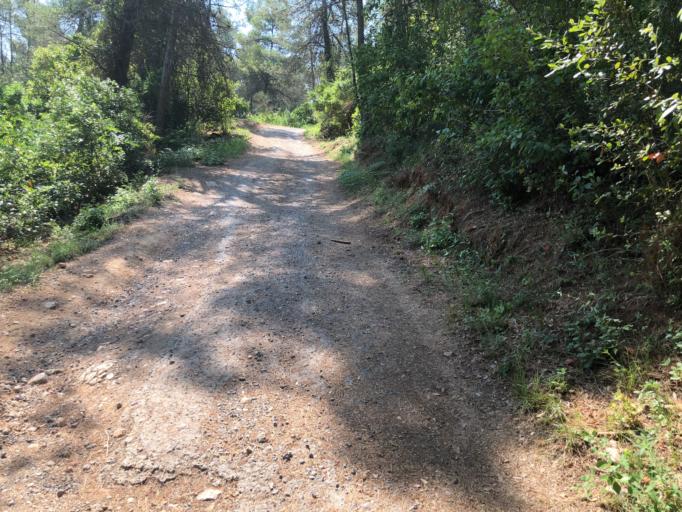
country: ES
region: Catalonia
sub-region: Provincia de Barcelona
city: Corbera de Llobregat
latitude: 41.4209
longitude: 1.9033
